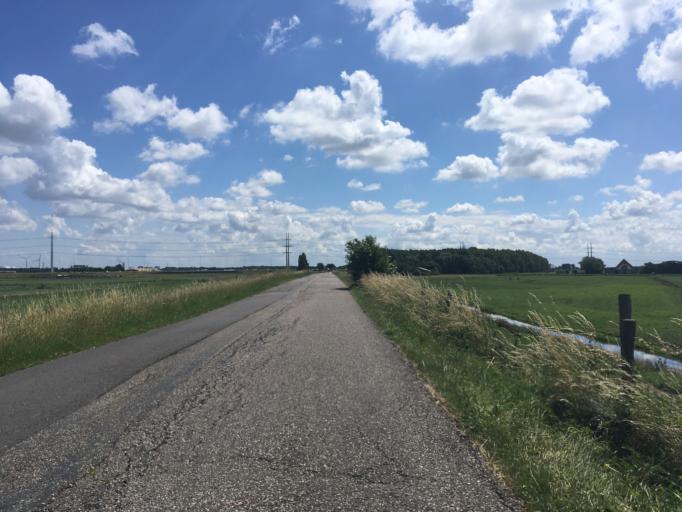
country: NL
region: North Holland
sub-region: Gemeente Haarlem
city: Haarlem
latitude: 52.4090
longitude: 4.6942
